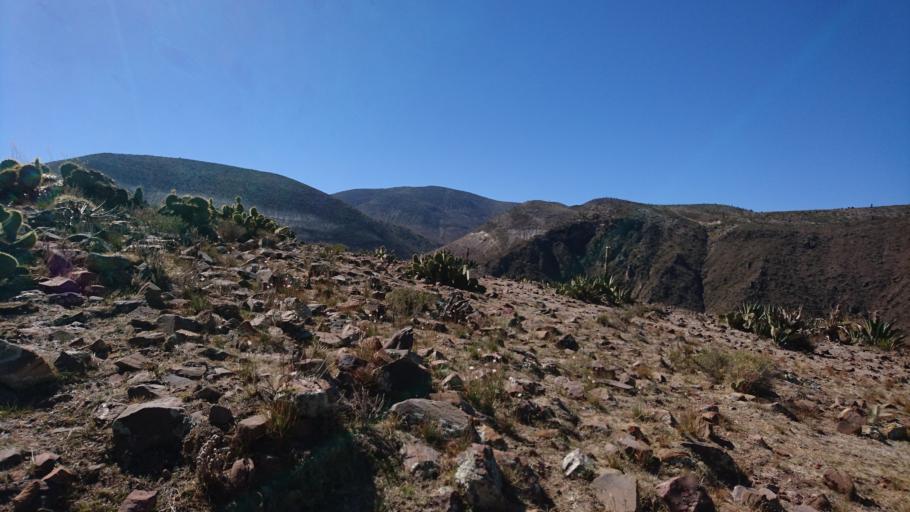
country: MX
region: San Luis Potosi
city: Matehuala
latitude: 23.6971
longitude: -100.8934
